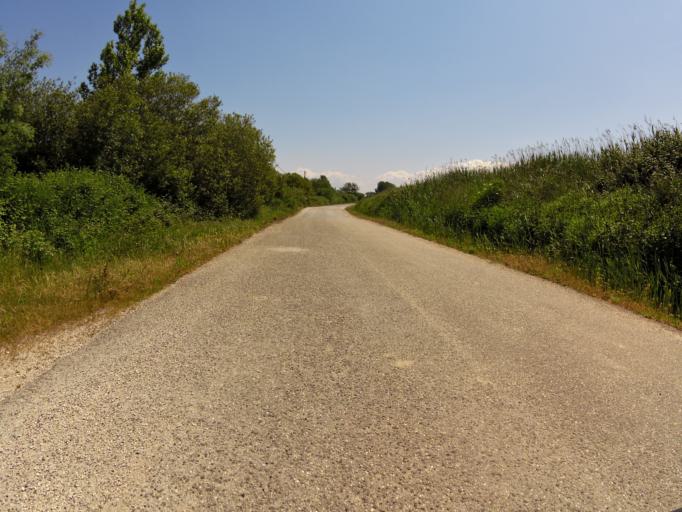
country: PT
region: Coimbra
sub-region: Montemor-O-Velho
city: Montemor-o-Velho
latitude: 40.1493
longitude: -8.7234
